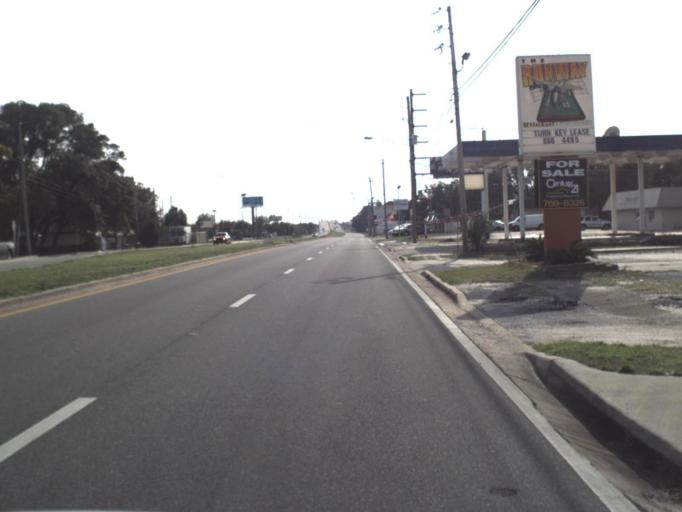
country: US
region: Florida
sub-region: Bay County
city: Parker
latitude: 30.1136
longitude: -85.6003
